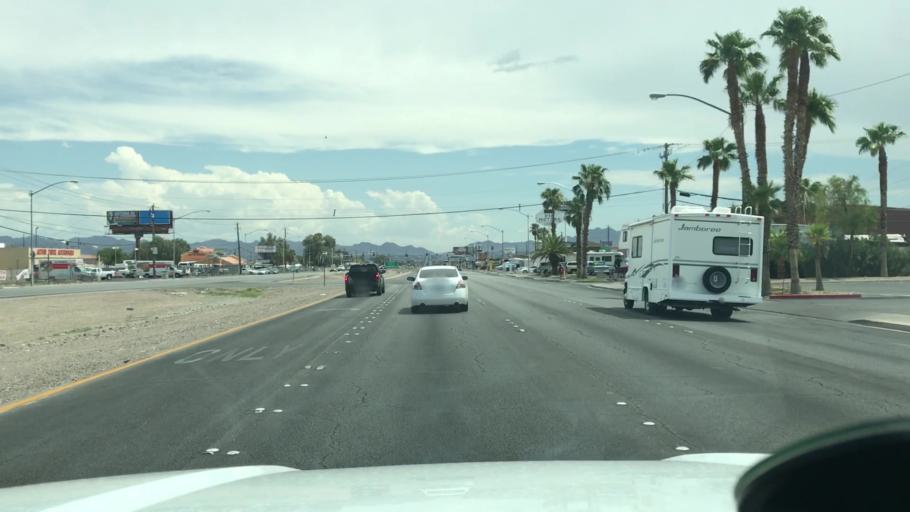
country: US
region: Nevada
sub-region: Clark County
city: Whitney
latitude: 36.0990
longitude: -115.0490
